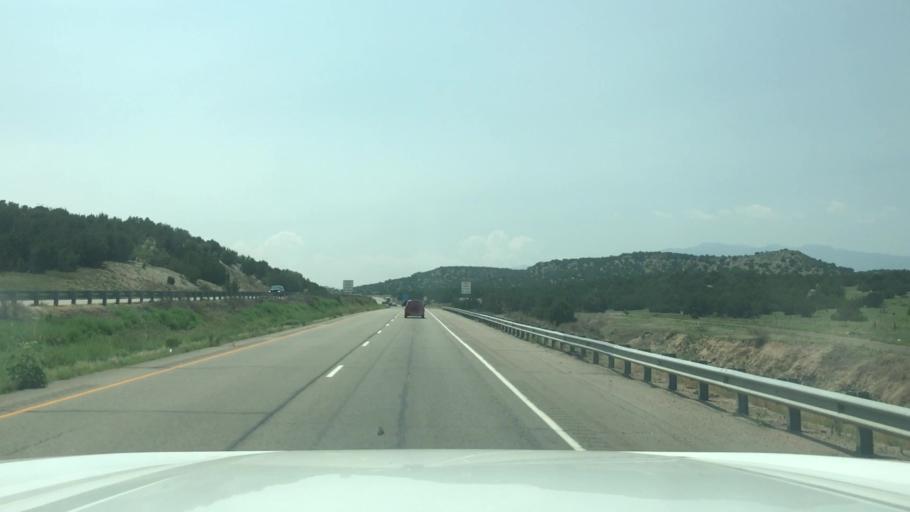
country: US
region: Colorado
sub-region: Pueblo County
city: Colorado City
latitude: 37.9908
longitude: -104.7669
